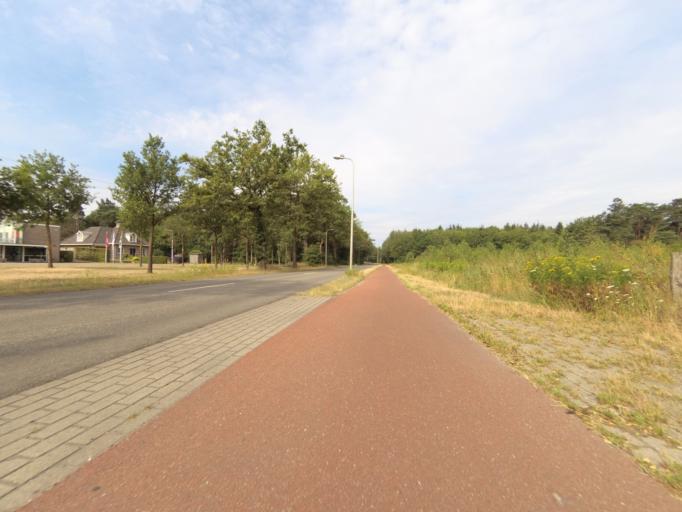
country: NL
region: Overijssel
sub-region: Gemeente Hengelo
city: Hengelo
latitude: 52.2164
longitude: 6.8111
